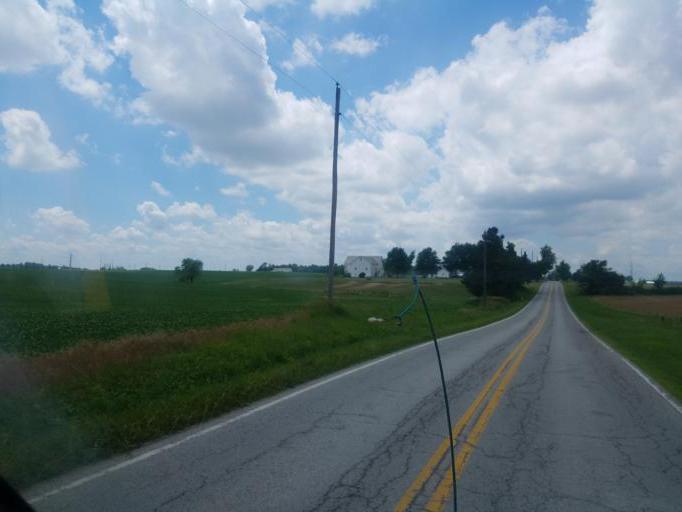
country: US
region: Ohio
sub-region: Huron County
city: Willard
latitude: 41.0551
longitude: -82.7749
